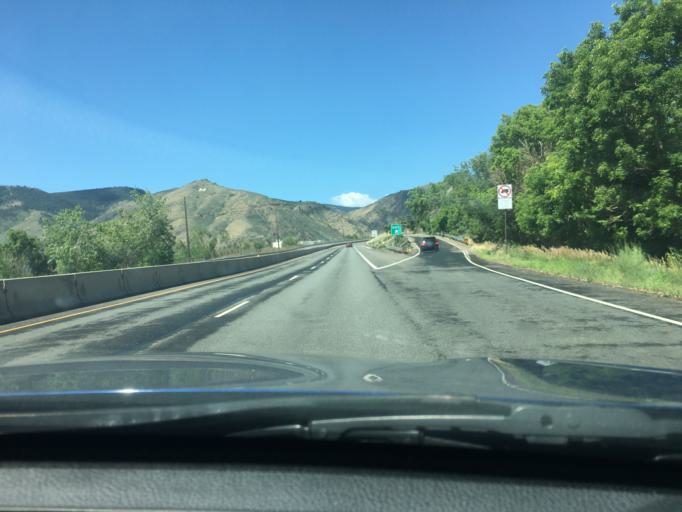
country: US
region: Colorado
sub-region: Jefferson County
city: Golden
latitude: 39.7631
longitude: -105.2172
